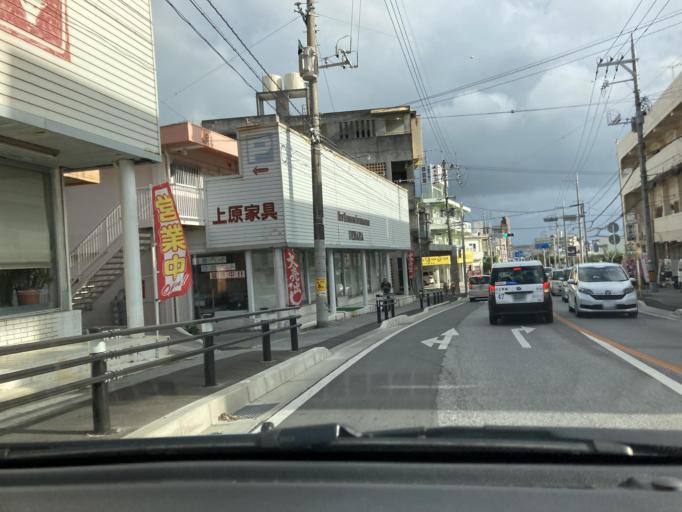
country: JP
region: Okinawa
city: Tomigusuku
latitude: 26.1797
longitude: 127.6646
